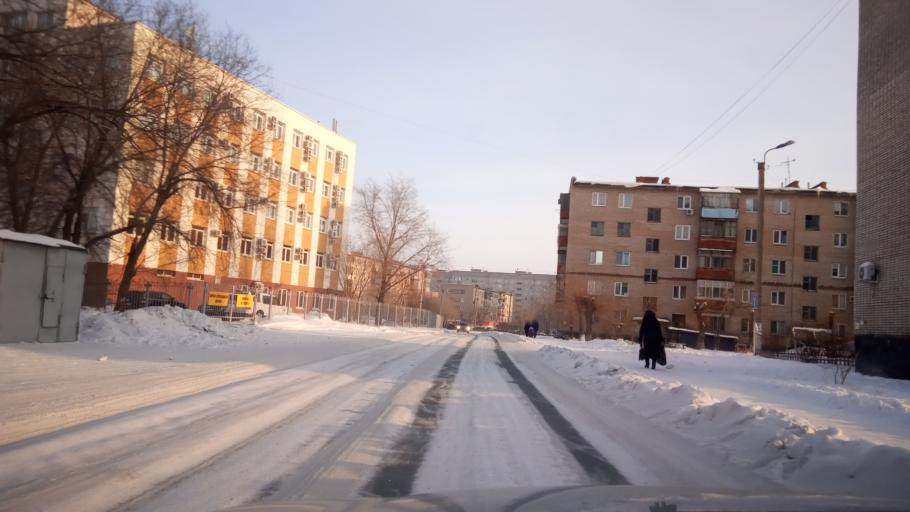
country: RU
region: Orenburg
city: Novotroitsk
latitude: 51.1950
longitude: 58.2877
